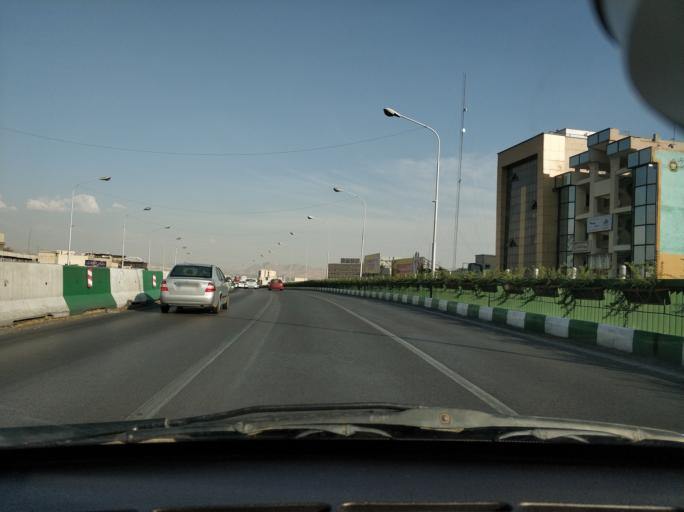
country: IR
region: Tehran
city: Tehran
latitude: 35.7422
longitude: 51.4453
